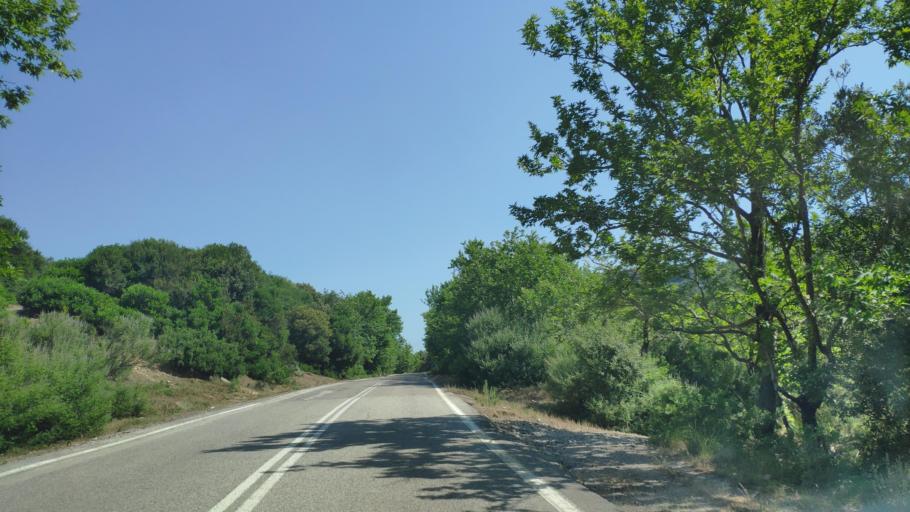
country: GR
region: West Greece
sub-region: Nomos Aitolias kai Akarnanias
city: Lepenou
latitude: 38.7853
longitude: 21.3338
